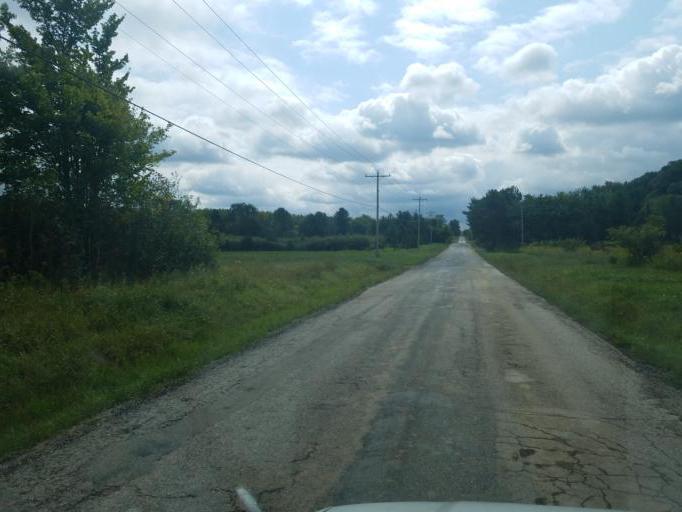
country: US
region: Ohio
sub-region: Geauga County
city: Chardon
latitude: 41.6513
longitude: -81.1127
